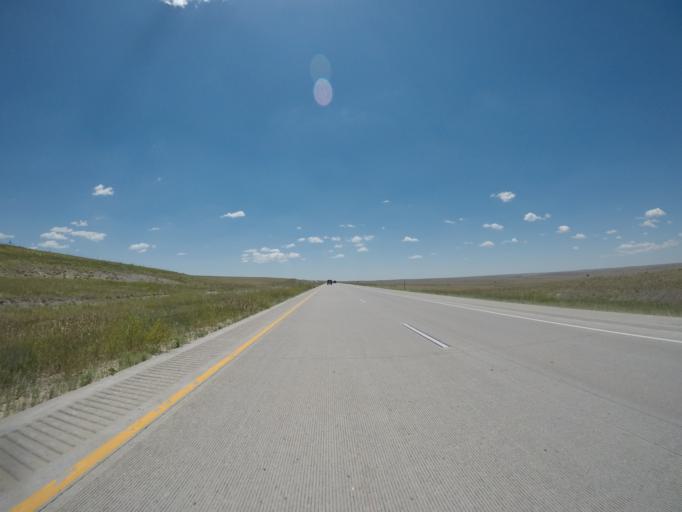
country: US
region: Colorado
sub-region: Lincoln County
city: Limon
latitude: 39.3865
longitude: -103.8917
